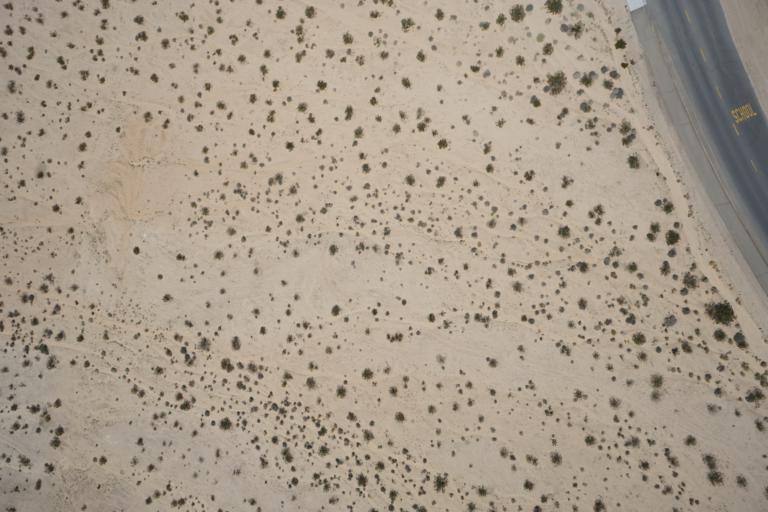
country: US
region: California
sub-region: San Bernardino County
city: Twentynine Palms
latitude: 34.1404
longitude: -116.0638
